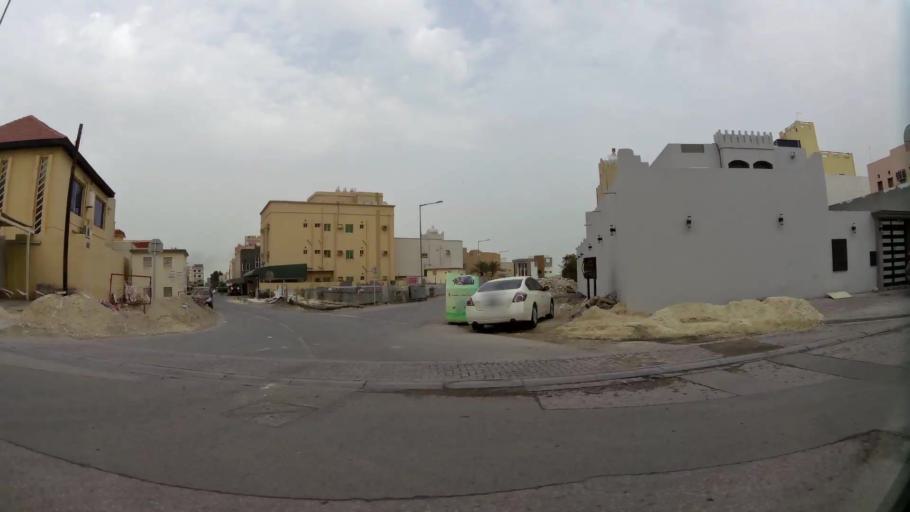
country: BH
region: Northern
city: Ar Rifa'
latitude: 26.1292
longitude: 50.5813
